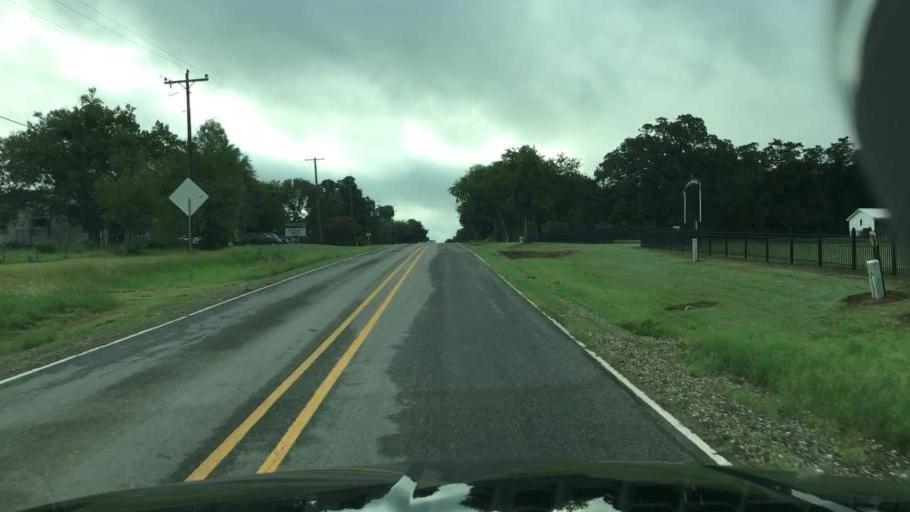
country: US
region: Texas
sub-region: Lee County
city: Lexington
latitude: 30.3643
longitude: -96.8340
